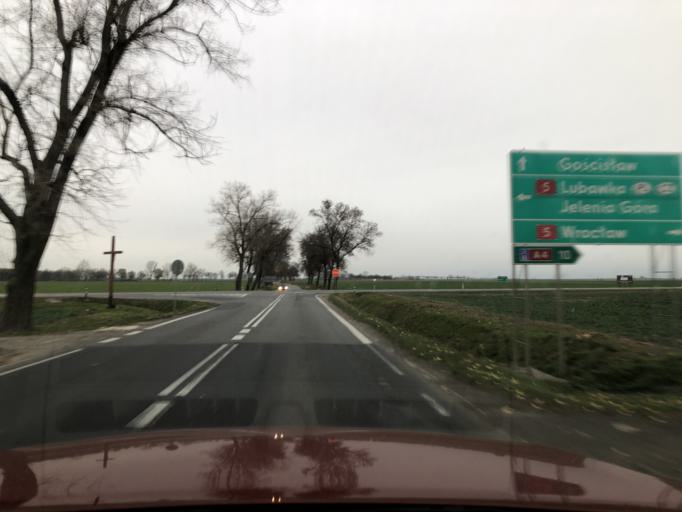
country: PL
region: Lower Silesian Voivodeship
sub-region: Powiat swidnicki
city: Zarow
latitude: 50.9937
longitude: 16.4883
